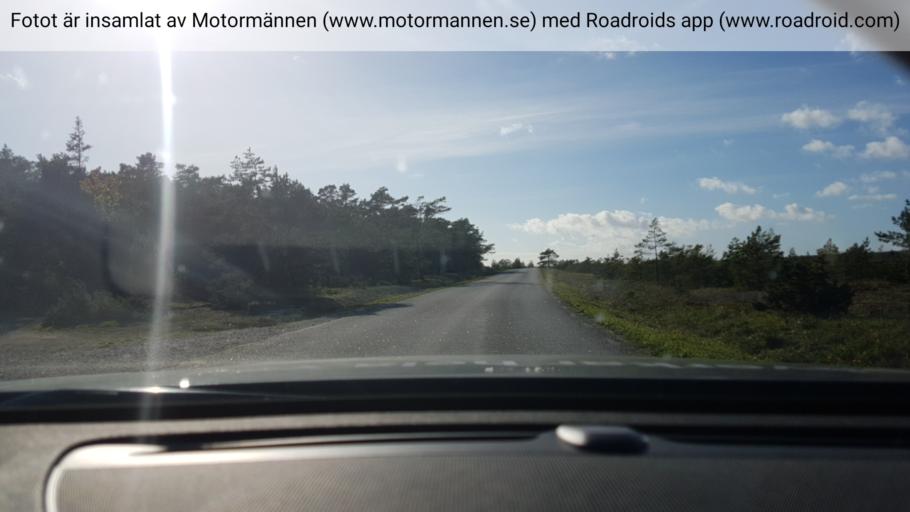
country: SE
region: Gotland
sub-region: Gotland
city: Slite
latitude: 57.8547
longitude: 18.8134
